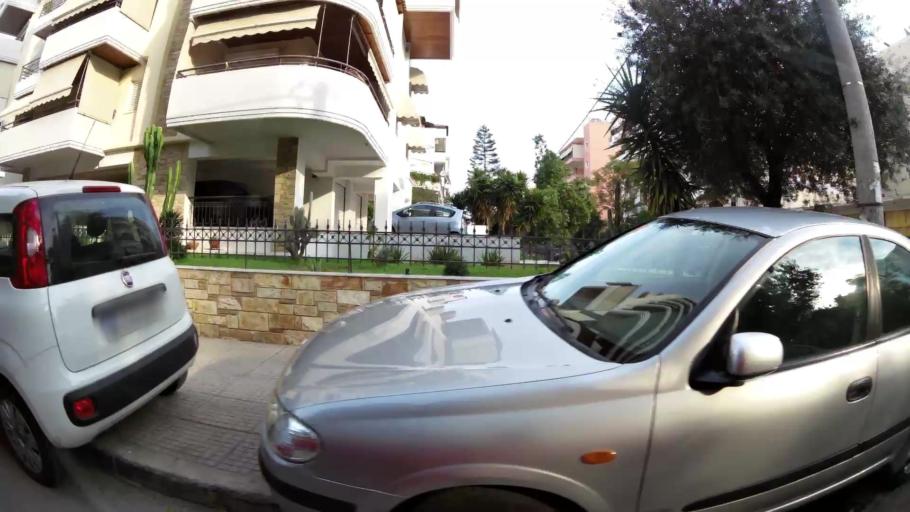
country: GR
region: Attica
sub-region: Nomarchia Athinas
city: Palaio Faliro
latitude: 37.9333
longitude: 23.6977
